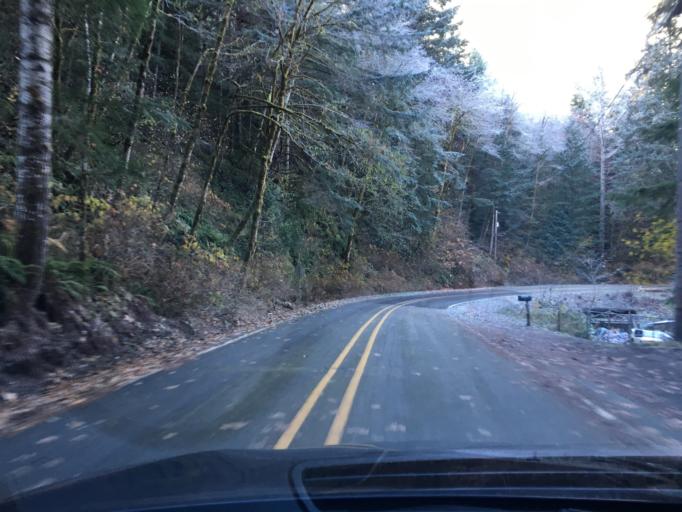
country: US
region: Oregon
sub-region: Douglas County
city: Winston
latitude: 43.3280
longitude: -123.5884
